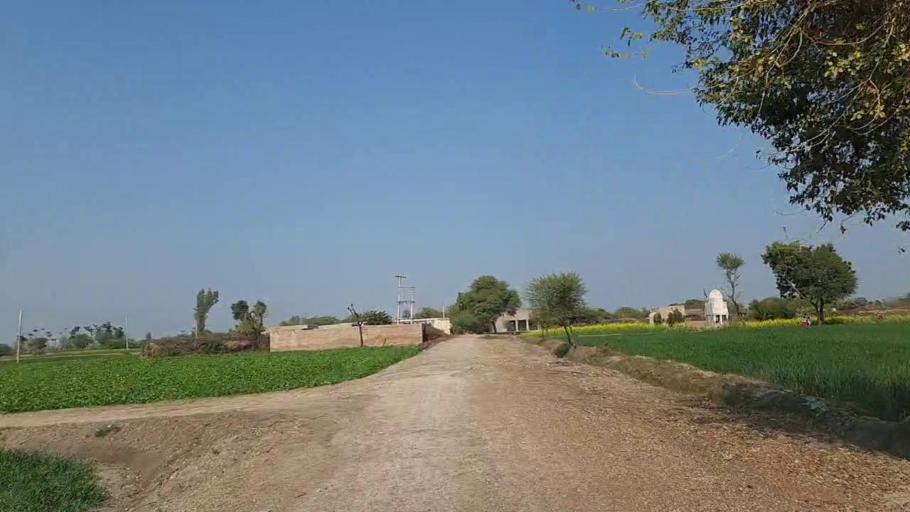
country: PK
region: Sindh
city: Jam Sahib
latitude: 26.2719
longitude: 68.5211
